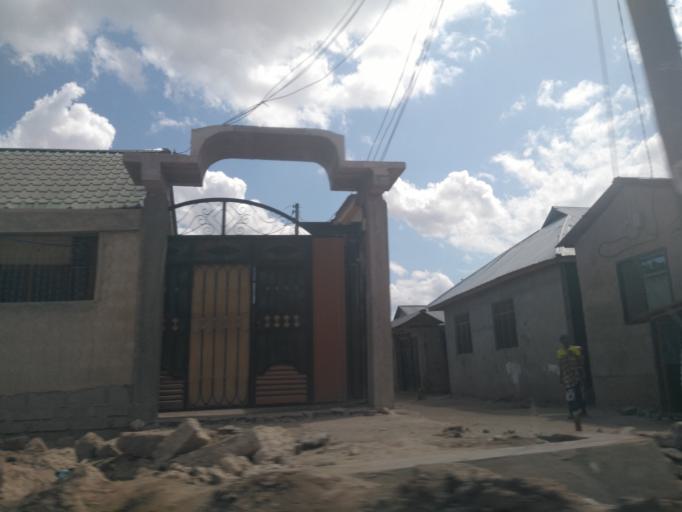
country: TZ
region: Dar es Salaam
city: Dar es Salaam
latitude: -6.8759
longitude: 39.2424
